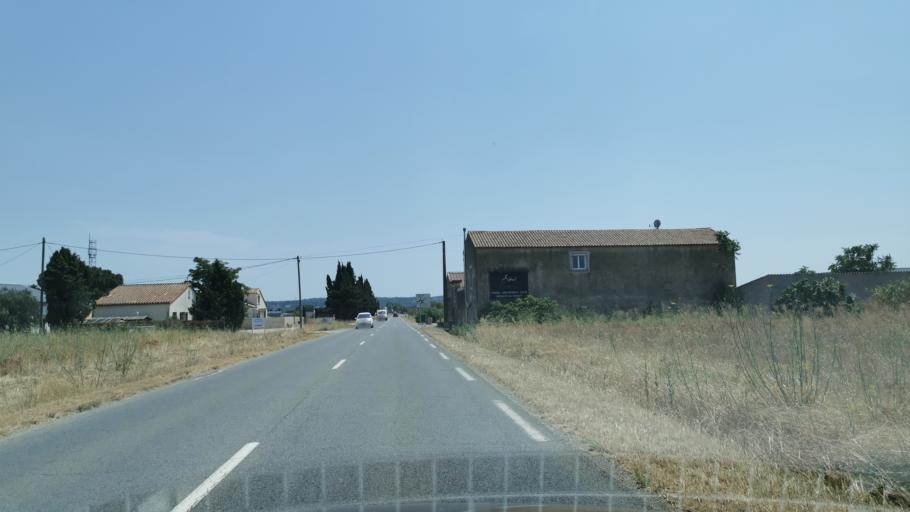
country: FR
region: Languedoc-Roussillon
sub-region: Departement de l'Aude
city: Saint-Marcel-sur-Aude
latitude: 43.2587
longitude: 2.9081
